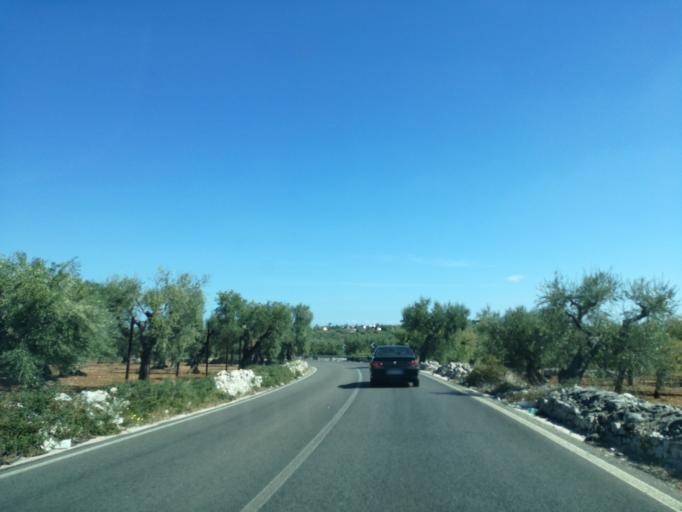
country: IT
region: Apulia
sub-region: Provincia di Bari
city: Castellana
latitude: 40.8950
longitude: 17.1891
